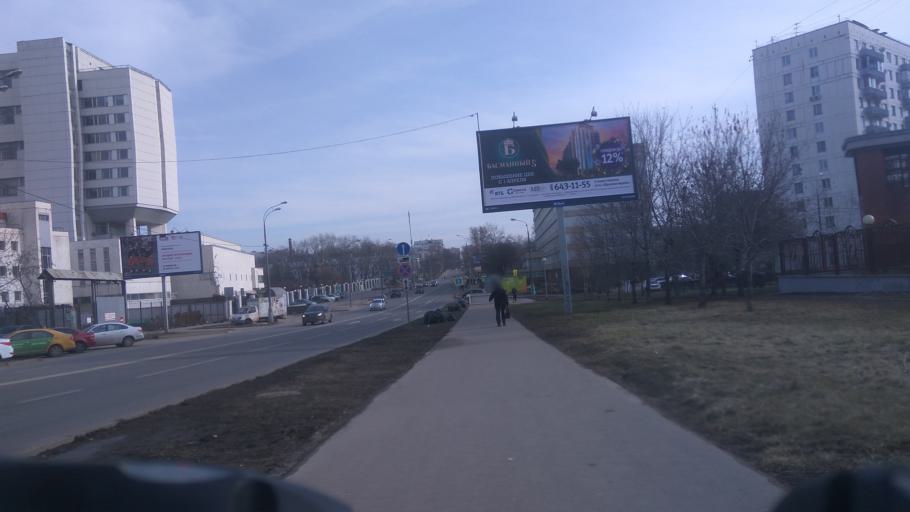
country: RU
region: Moscow
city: Lefortovo
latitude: 55.7714
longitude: 37.6885
